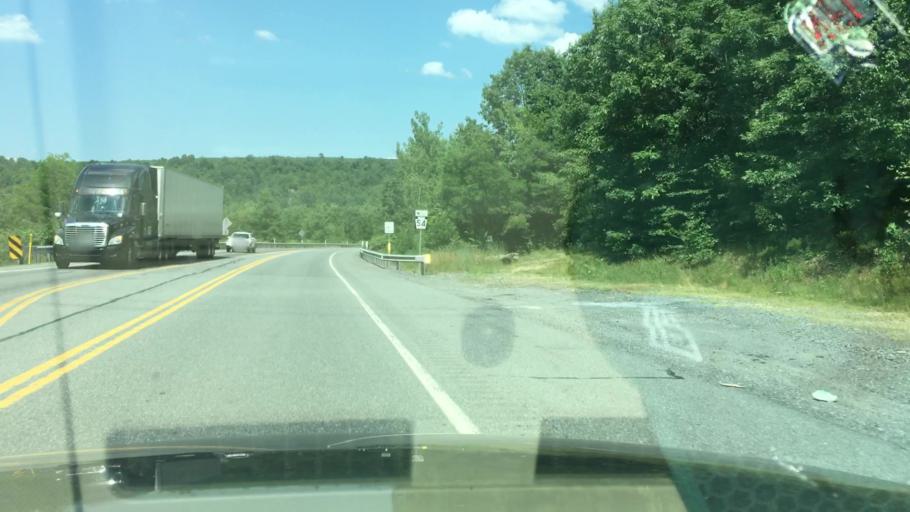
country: US
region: Pennsylvania
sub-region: Northumberland County
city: Kulpmont
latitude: 40.7862
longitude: -76.4473
